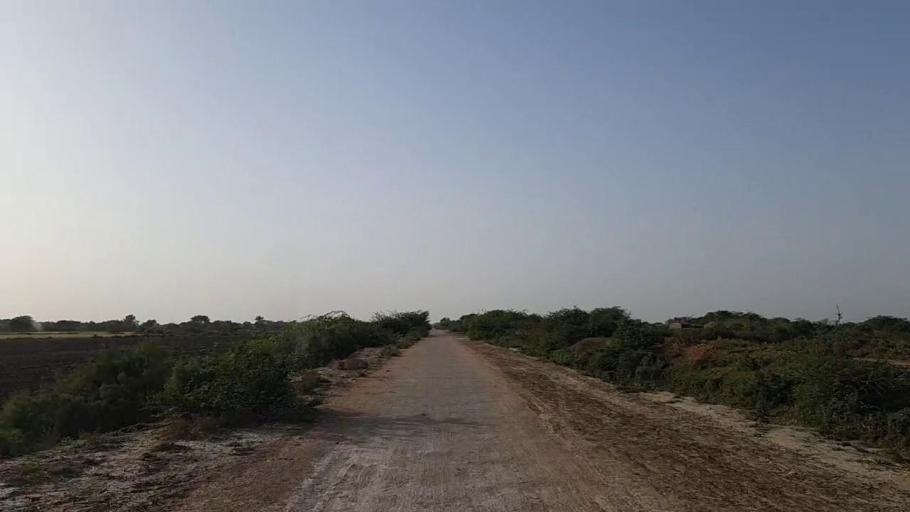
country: PK
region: Sindh
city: Jati
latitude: 24.3320
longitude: 68.1574
